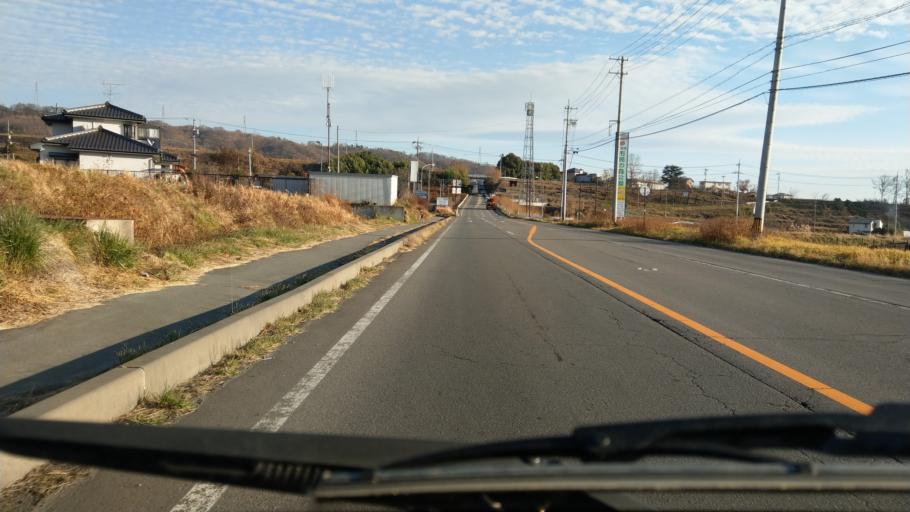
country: JP
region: Nagano
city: Ueda
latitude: 36.3959
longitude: 138.2973
